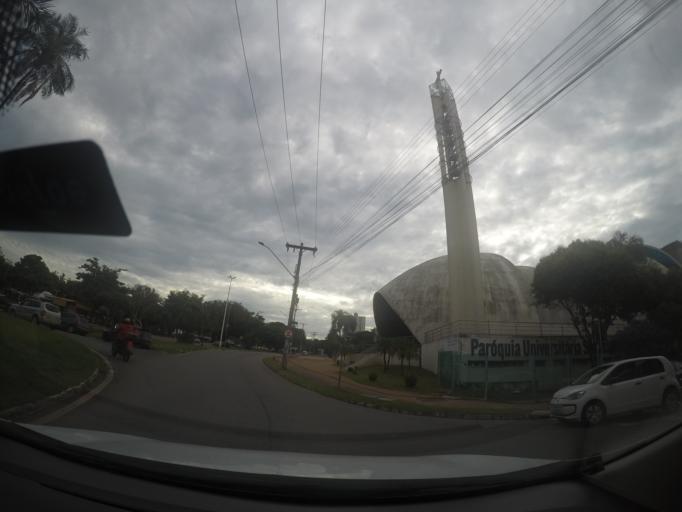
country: BR
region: Goias
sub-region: Goiania
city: Goiania
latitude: -16.6780
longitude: -49.2447
